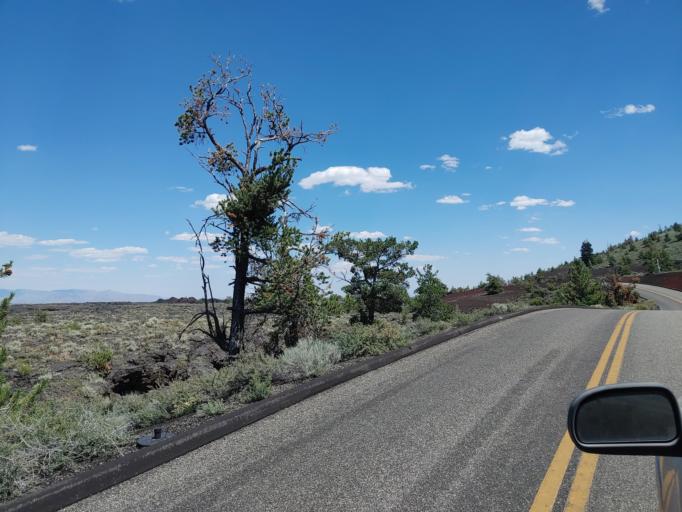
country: US
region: Idaho
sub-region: Butte County
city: Arco
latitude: 43.4536
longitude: -113.5564
